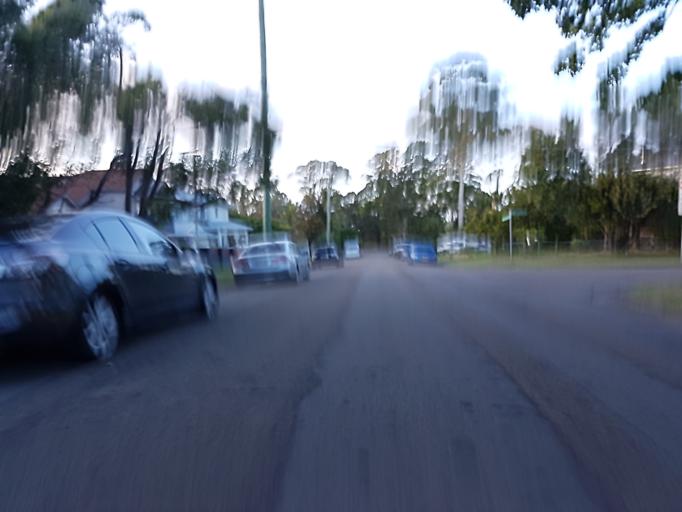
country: AU
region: New South Wales
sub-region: Warringah
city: Killarney Heights
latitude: -33.7575
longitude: 151.2295
